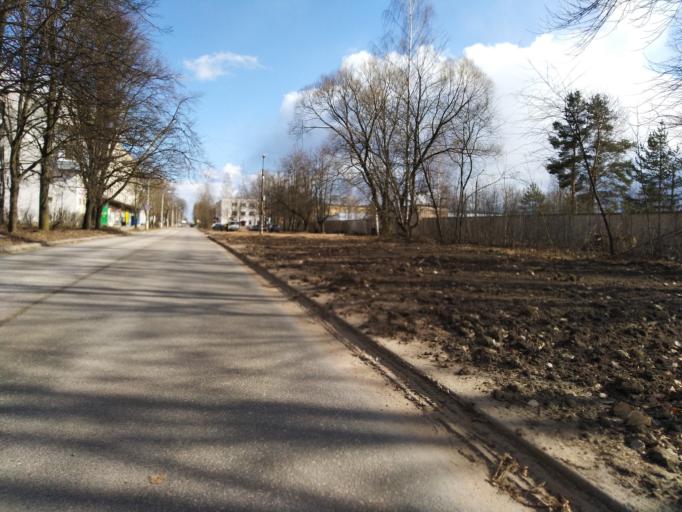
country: RU
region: Leningrad
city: Novoye Devyatkino
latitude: 60.1083
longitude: 30.4835
